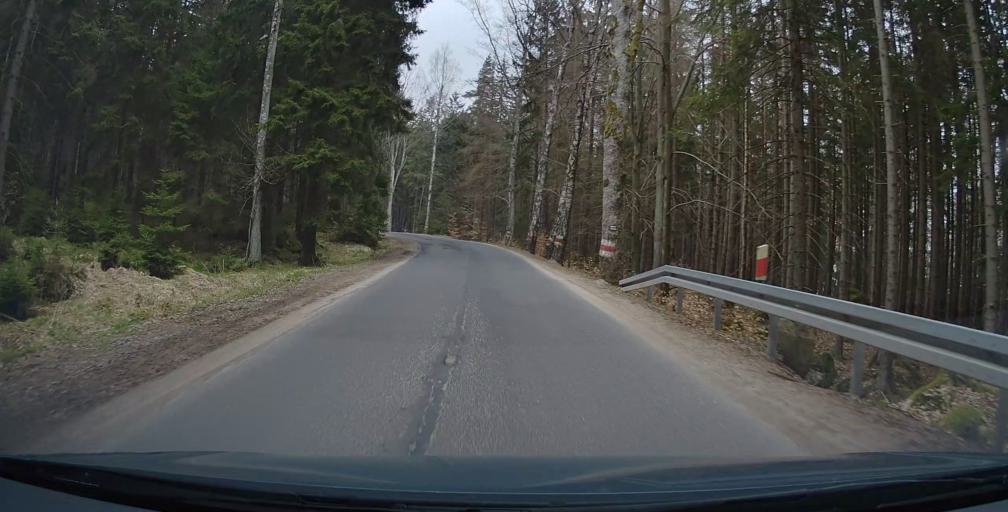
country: PL
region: Lower Silesian Voivodeship
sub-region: Powiat klodzki
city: Radkow
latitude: 50.4763
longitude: 16.3924
